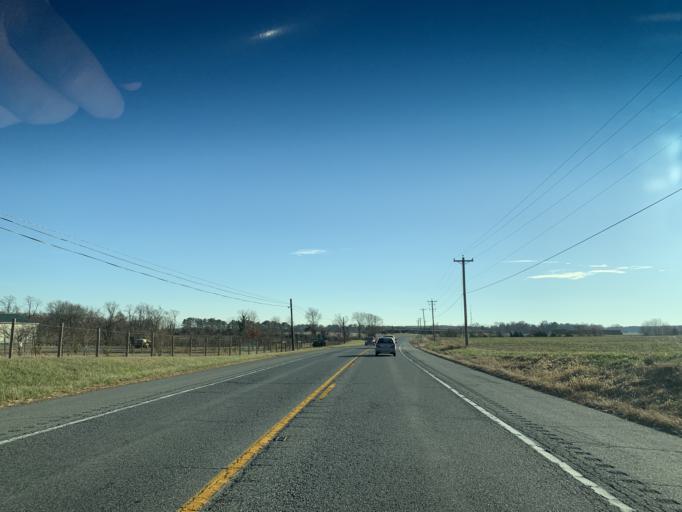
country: US
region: Delaware
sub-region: New Castle County
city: Middletown
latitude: 39.4199
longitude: -75.8608
